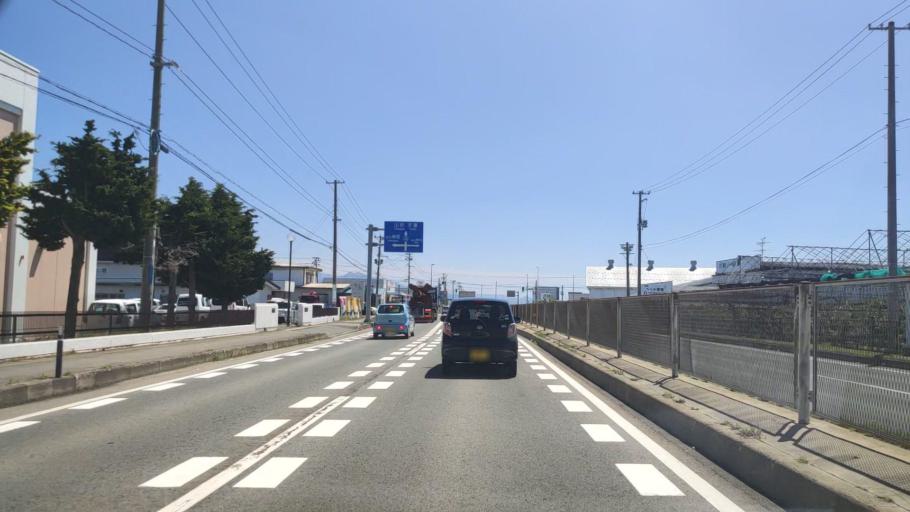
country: JP
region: Yamagata
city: Higashine
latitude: 38.4197
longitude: 140.3755
